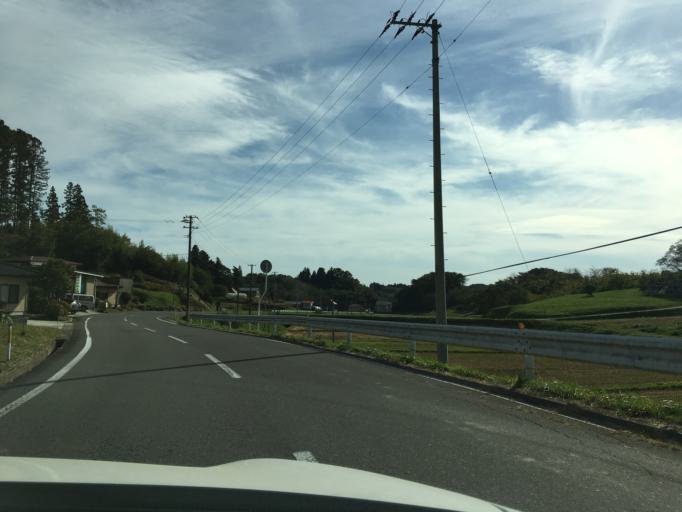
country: JP
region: Fukushima
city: Miharu
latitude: 37.4742
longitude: 140.4929
